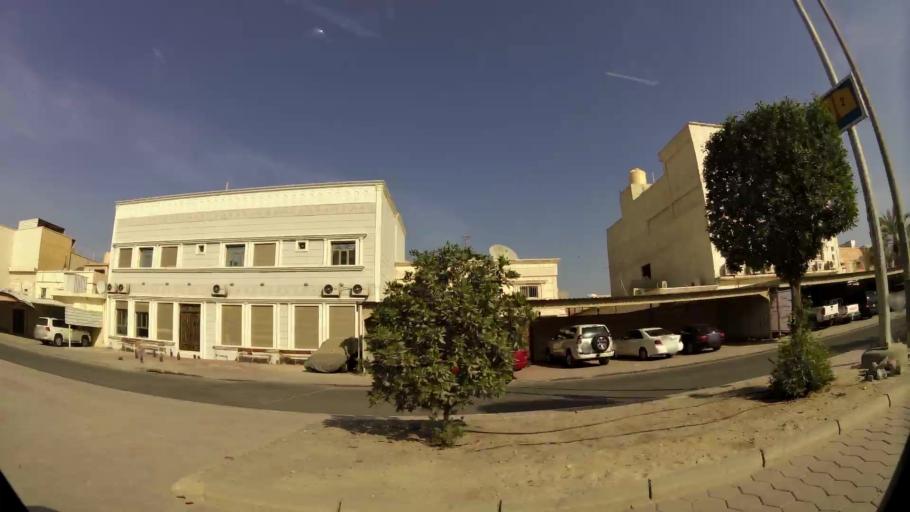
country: KW
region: Al Ahmadi
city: Ar Riqqah
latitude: 29.1531
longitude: 48.1046
